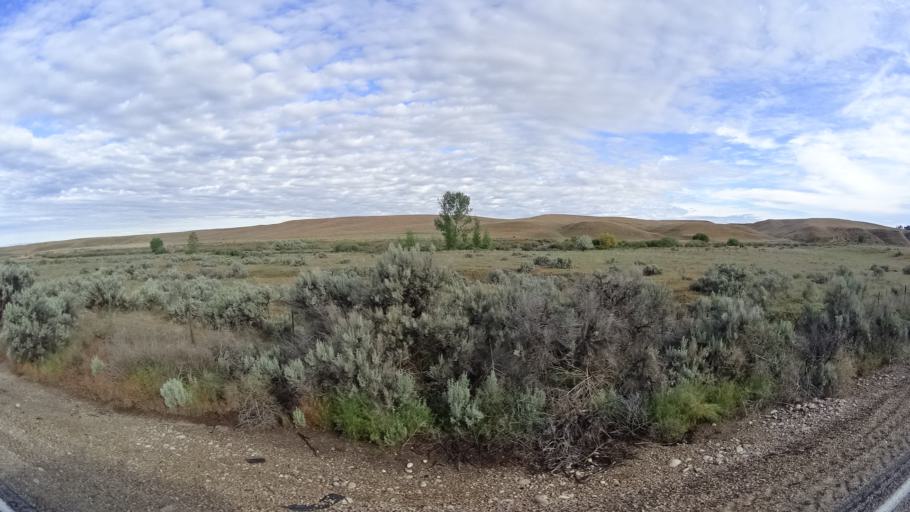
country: US
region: Idaho
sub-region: Ada County
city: Star
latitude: 43.7678
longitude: -116.4969
